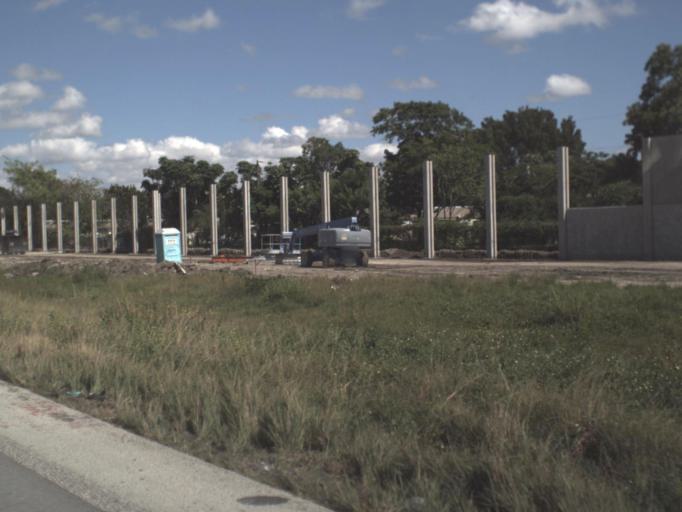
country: US
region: Florida
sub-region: Miami-Dade County
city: South Miami Heights
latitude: 25.6090
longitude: -80.3780
